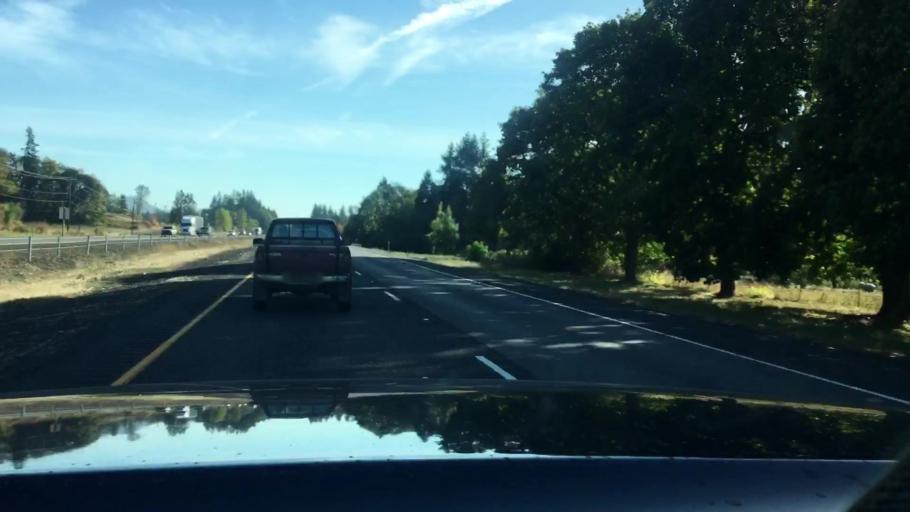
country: US
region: Oregon
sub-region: Lane County
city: Creswell
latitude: 43.8651
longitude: -123.0147
